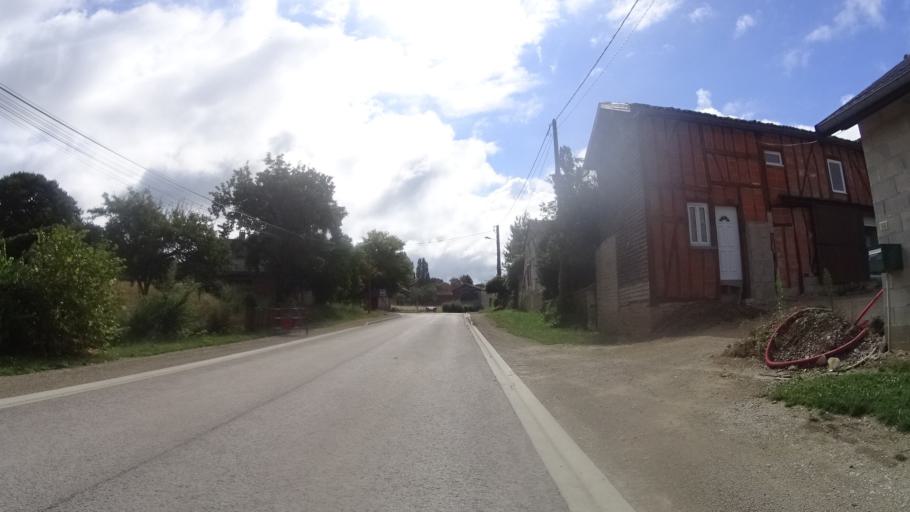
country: FR
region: Champagne-Ardenne
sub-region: Departement de l'Aube
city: Brienne-le-Chateau
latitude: 48.3450
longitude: 4.6049
